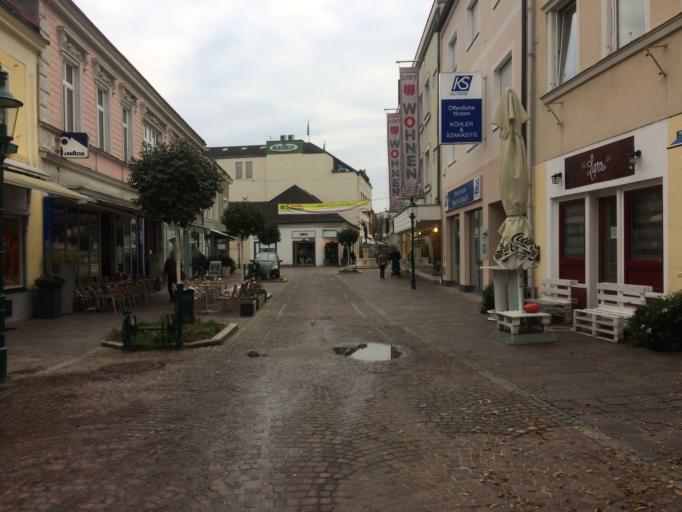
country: AT
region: Lower Austria
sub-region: Politischer Bezirk Tulln
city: Tulln
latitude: 48.3319
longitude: 16.0533
